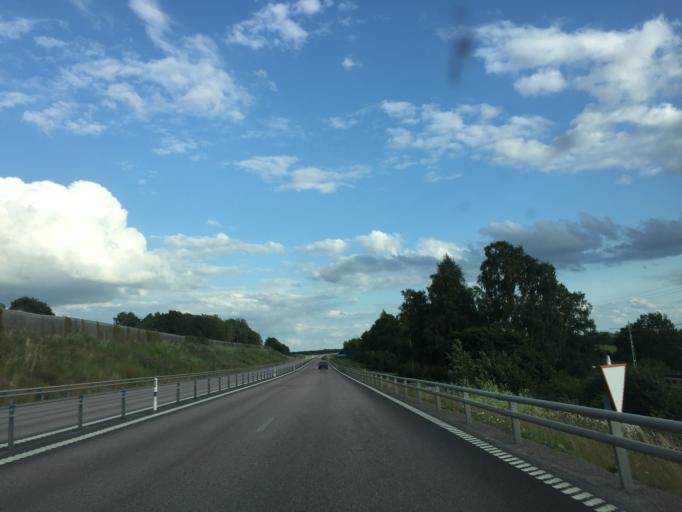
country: SE
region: OEstergoetland
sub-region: Motala Kommun
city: Motala
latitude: 58.5147
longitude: 15.0162
